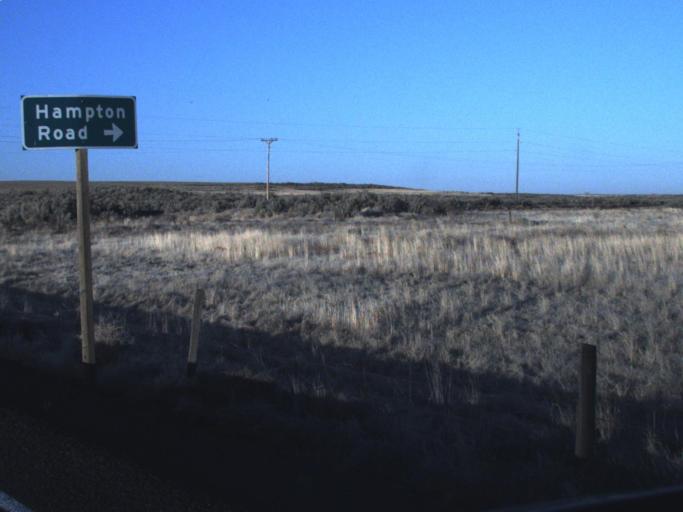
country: US
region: Washington
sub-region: Franklin County
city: Connell
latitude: 46.7794
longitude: -118.5474
